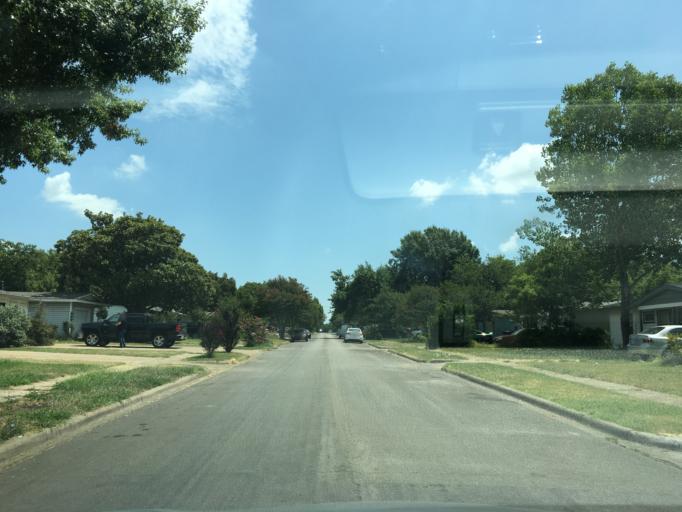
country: US
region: Texas
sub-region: Dallas County
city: Garland
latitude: 32.8600
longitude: -96.6813
